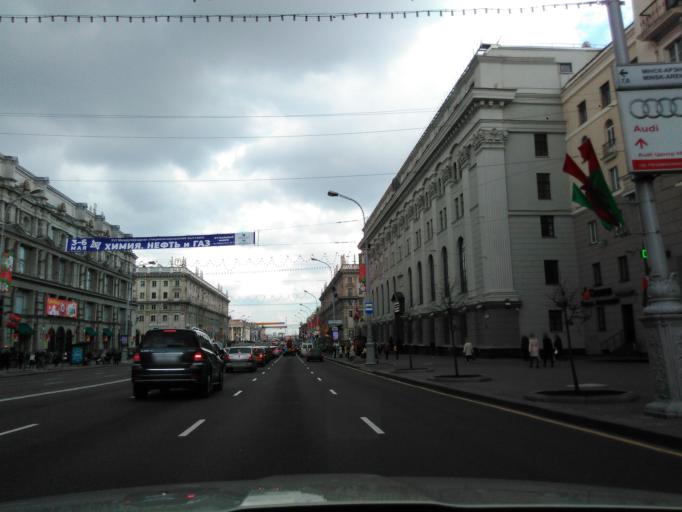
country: BY
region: Minsk
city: Minsk
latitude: 53.8997
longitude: 27.5574
